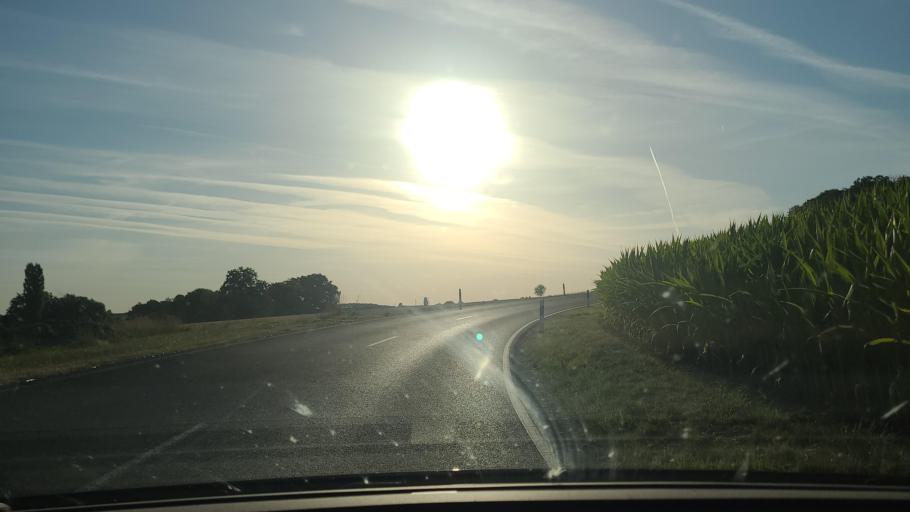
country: LU
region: Luxembourg
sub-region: Canton de Capellen
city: Garnich
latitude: 49.6138
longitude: 5.9647
